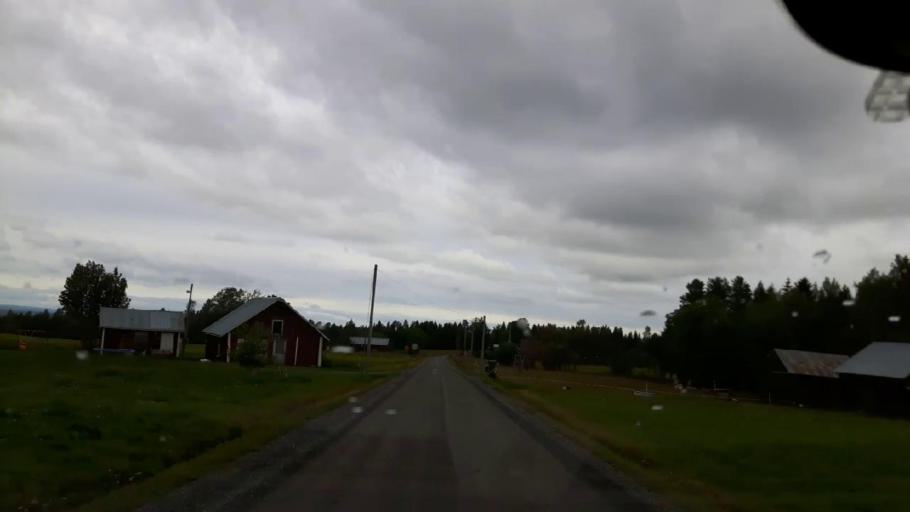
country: SE
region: Jaemtland
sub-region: OEstersunds Kommun
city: Ostersund
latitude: 63.0561
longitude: 14.5606
